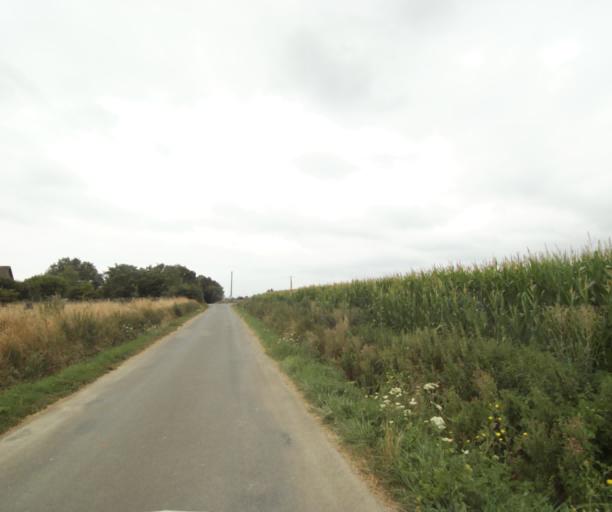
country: FR
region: Pays de la Loire
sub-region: Departement de la Sarthe
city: Solesmes
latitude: 47.8586
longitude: -0.3036
